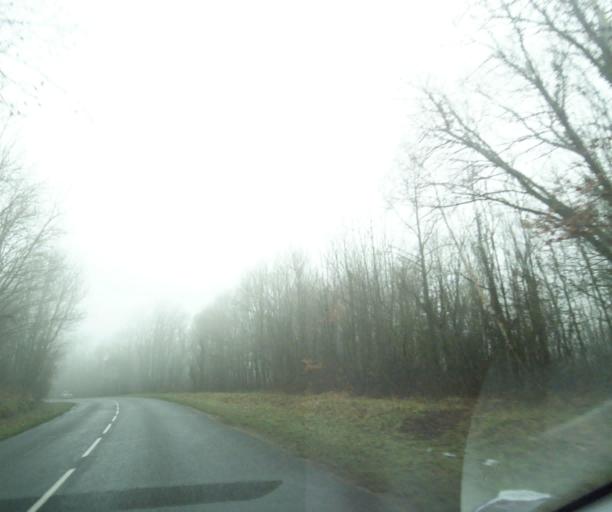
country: FR
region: Ile-de-France
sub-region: Departement de Seine-et-Marne
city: Saint-Mard
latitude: 49.0467
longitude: 2.6886
